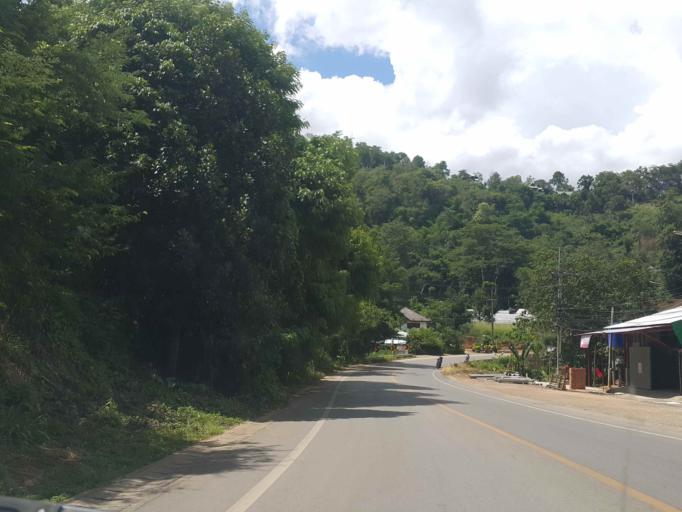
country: TH
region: Chiang Mai
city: Samoeng
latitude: 18.8851
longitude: 98.8209
